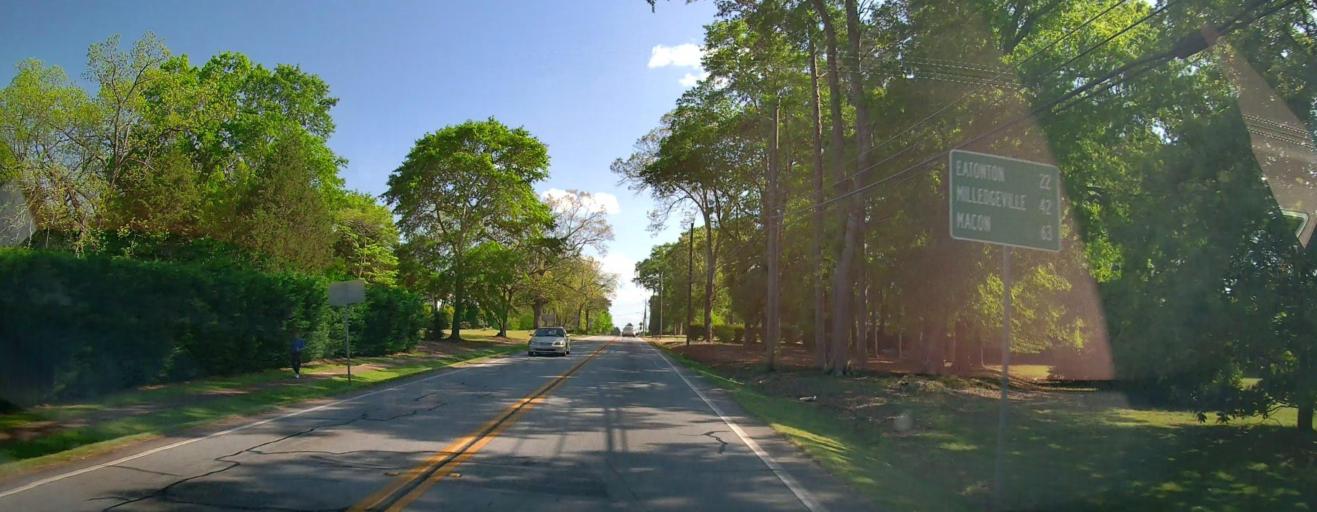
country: US
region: Georgia
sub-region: Morgan County
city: Madison
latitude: 33.5857
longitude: -83.4776
